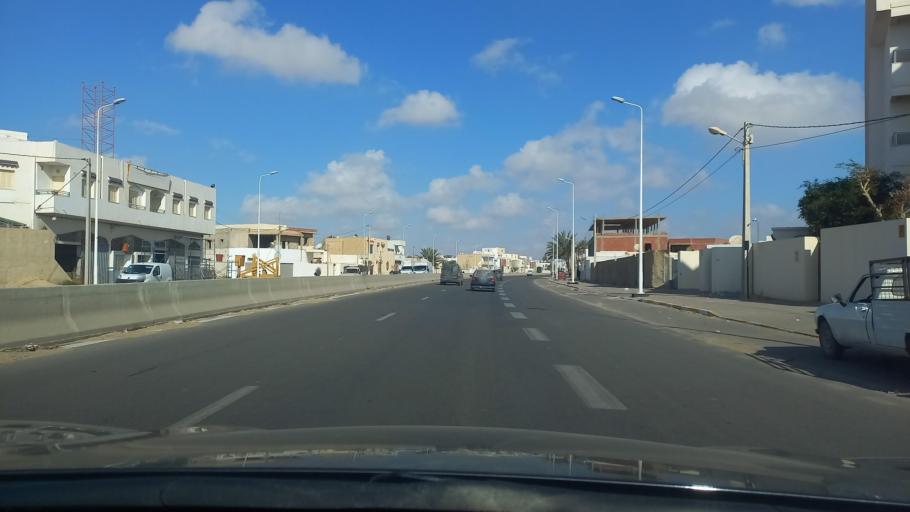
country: TN
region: Safaqis
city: Sfax
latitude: 34.7400
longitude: 10.7238
